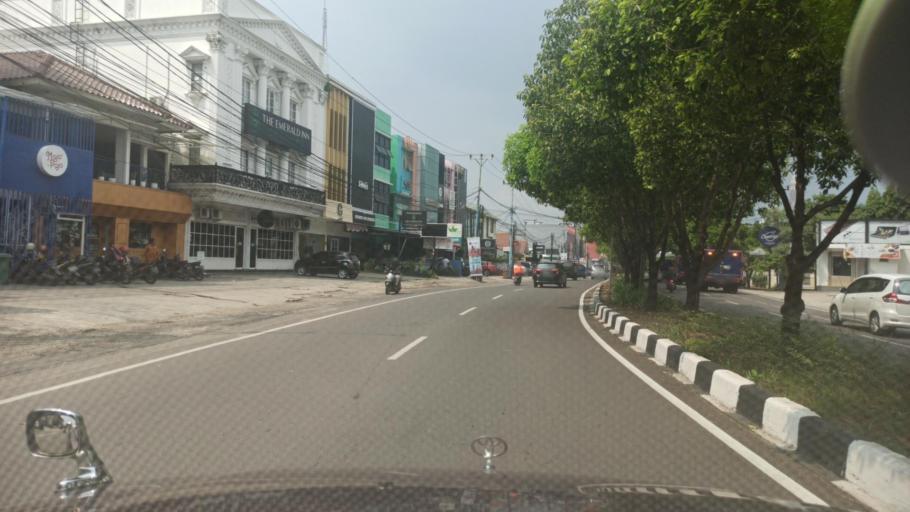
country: ID
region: South Sumatra
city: Palembang
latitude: -2.9760
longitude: 104.7373
